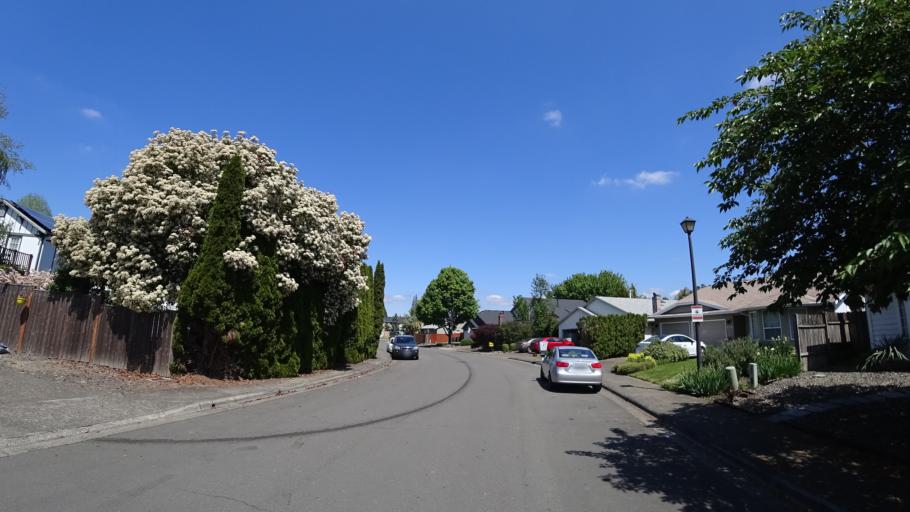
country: US
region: Oregon
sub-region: Washington County
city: Aloha
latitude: 45.5126
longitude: -122.8999
